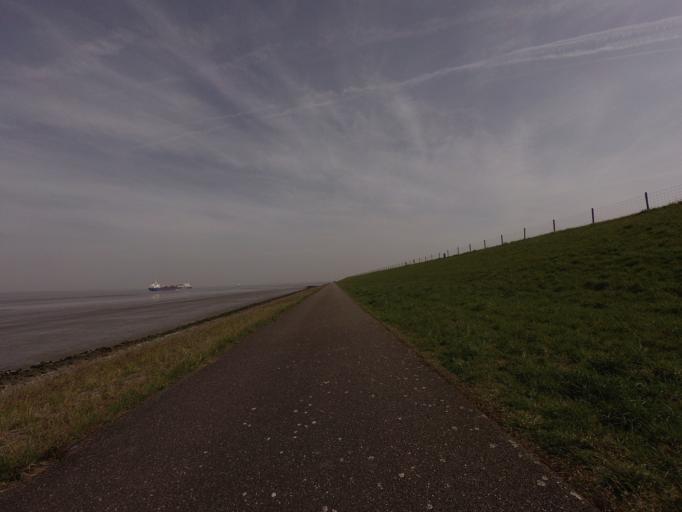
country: NL
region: Zeeland
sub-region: Gemeente Hulst
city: Hulst
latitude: 51.3641
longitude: 4.0806
